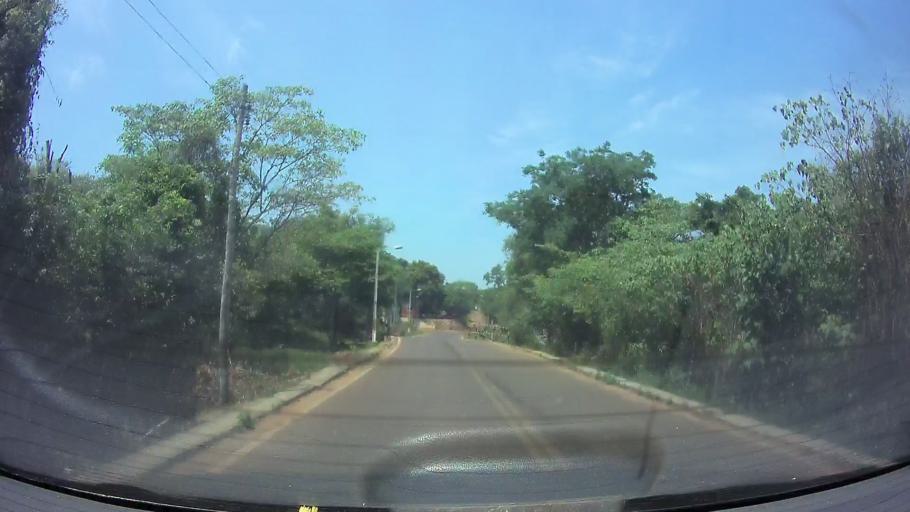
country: PY
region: Central
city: Ita
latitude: -25.4405
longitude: -57.4021
